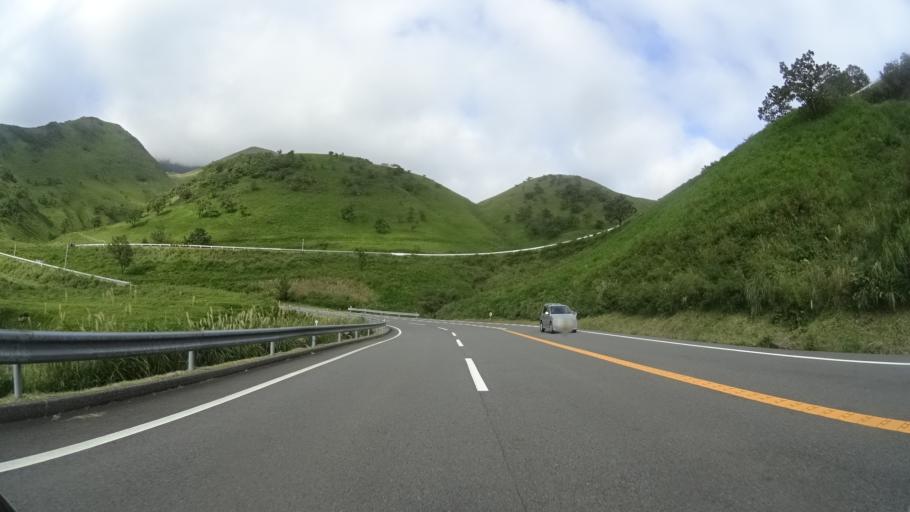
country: JP
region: Oita
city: Beppu
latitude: 33.2626
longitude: 131.3830
